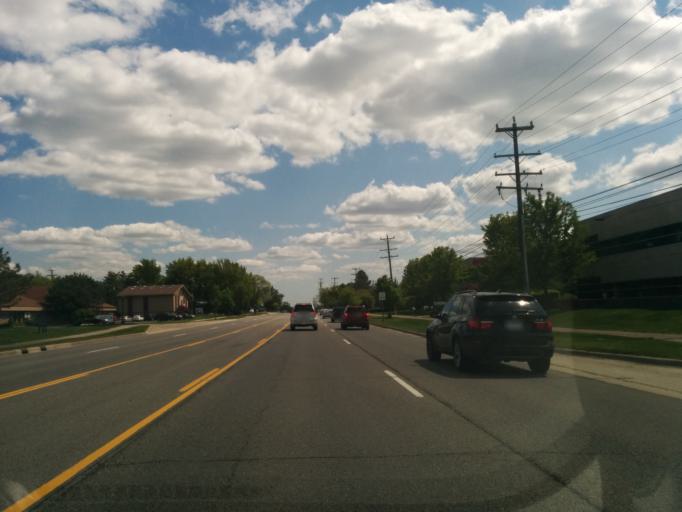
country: US
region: Michigan
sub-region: Oakland County
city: Farmington Hills
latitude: 42.5204
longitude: -83.3598
